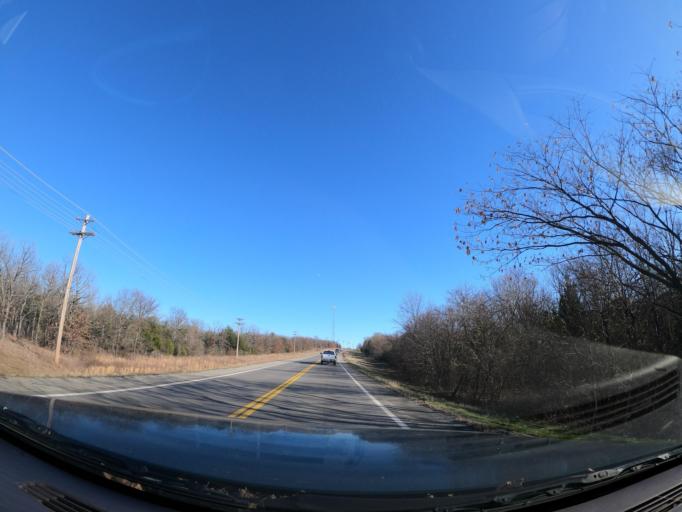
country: US
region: Oklahoma
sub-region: Pittsburg County
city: Longtown
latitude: 35.2382
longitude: -95.4702
